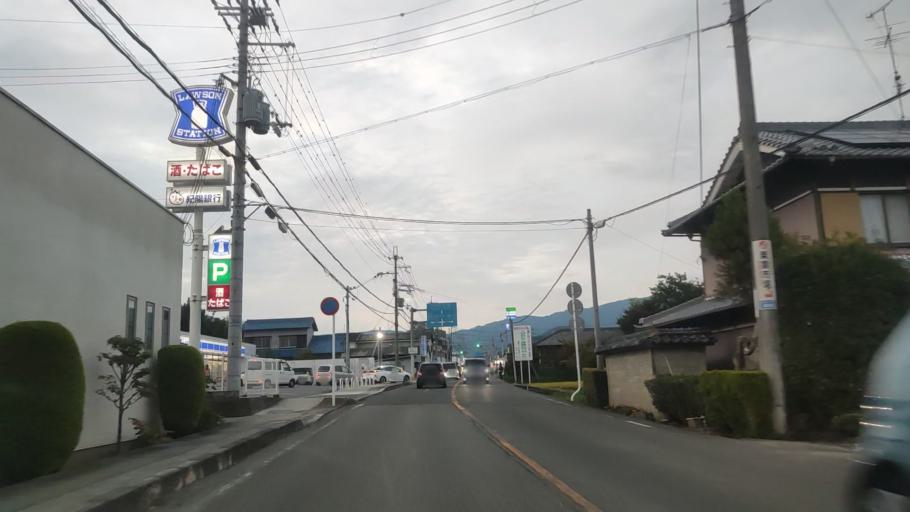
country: JP
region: Wakayama
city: Hashimoto
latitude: 34.3368
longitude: 135.6057
